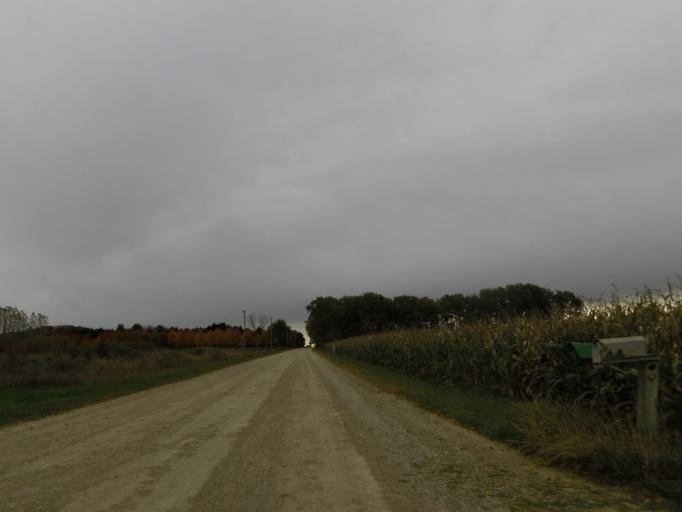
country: US
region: Minnesota
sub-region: Scott County
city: Prior Lake
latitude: 44.7035
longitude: -93.5119
